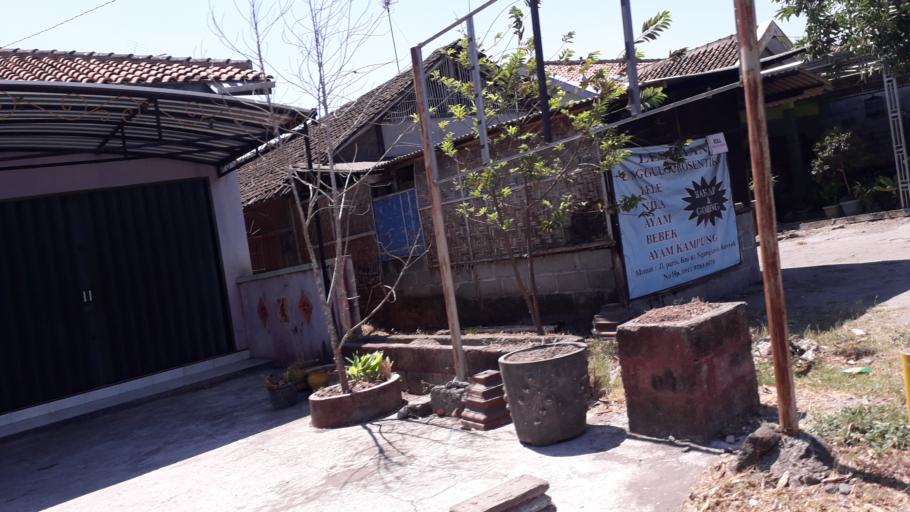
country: ID
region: Daerah Istimewa Yogyakarta
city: Pundong
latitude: -7.9778
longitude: 110.3175
